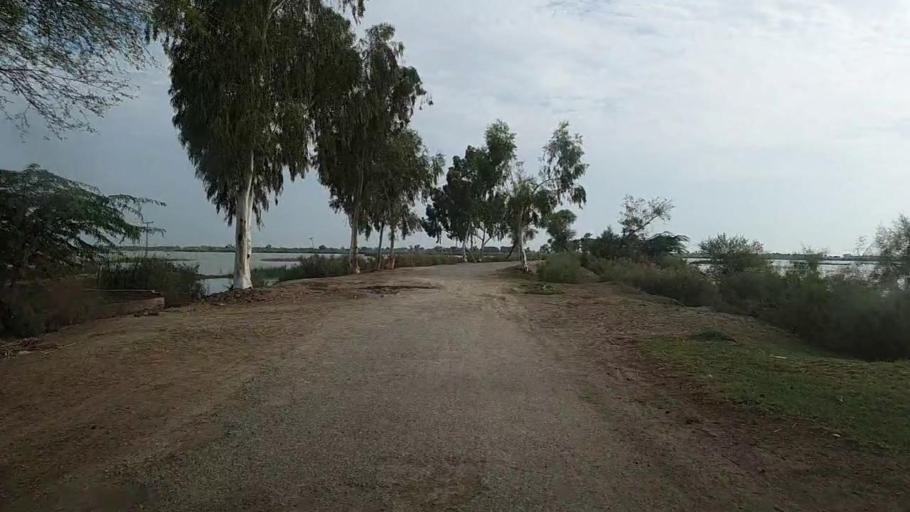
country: PK
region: Sindh
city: Thul
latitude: 28.2804
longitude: 68.8558
